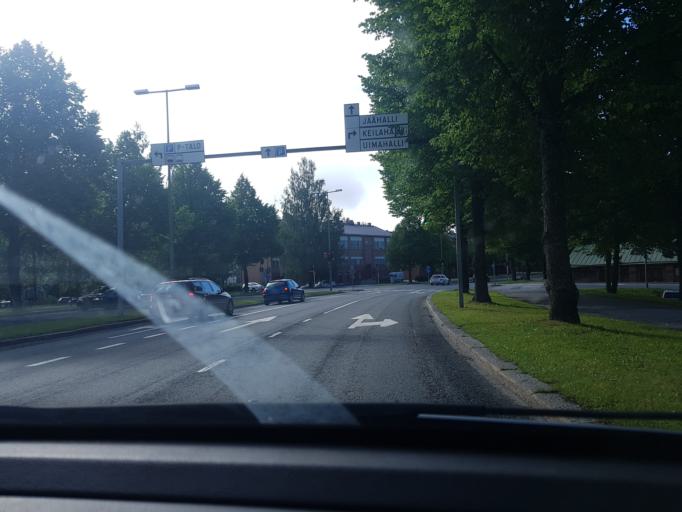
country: FI
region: Northern Savo
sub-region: Kuopio
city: Kuopio
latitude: 62.8970
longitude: 27.6689
